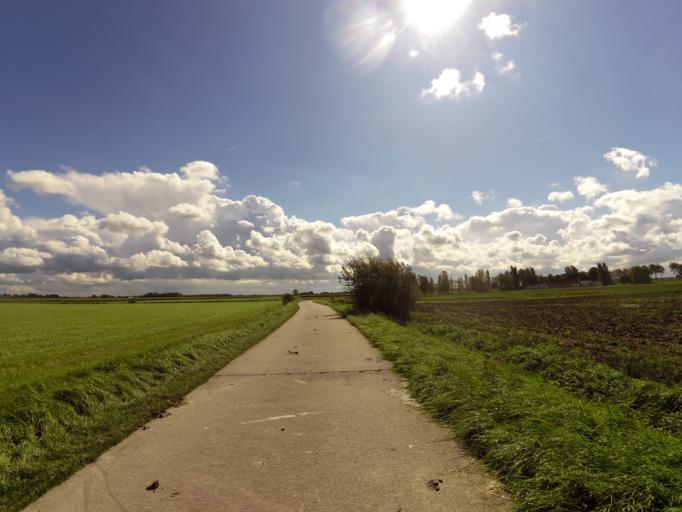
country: BE
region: Flanders
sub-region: Provincie West-Vlaanderen
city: Middelkerke
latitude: 51.1541
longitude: 2.8671
